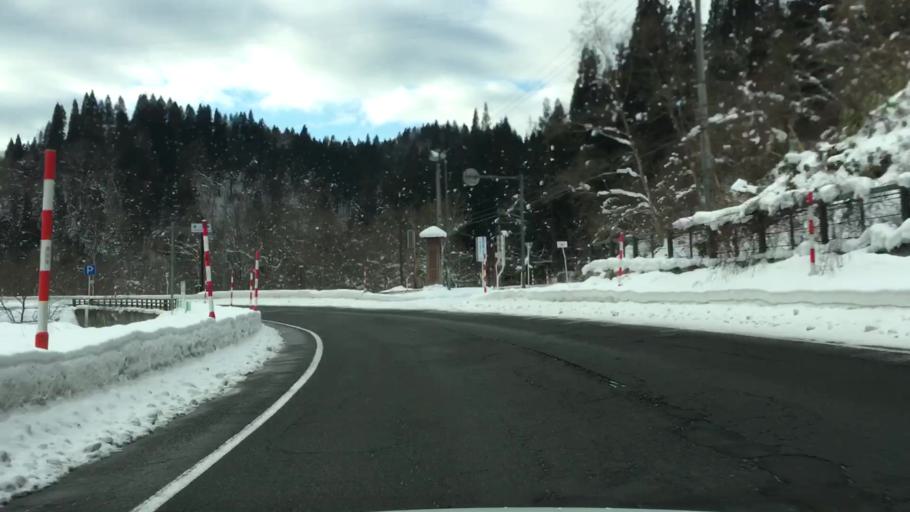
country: JP
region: Akita
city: Odate
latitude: 40.4346
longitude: 140.6349
